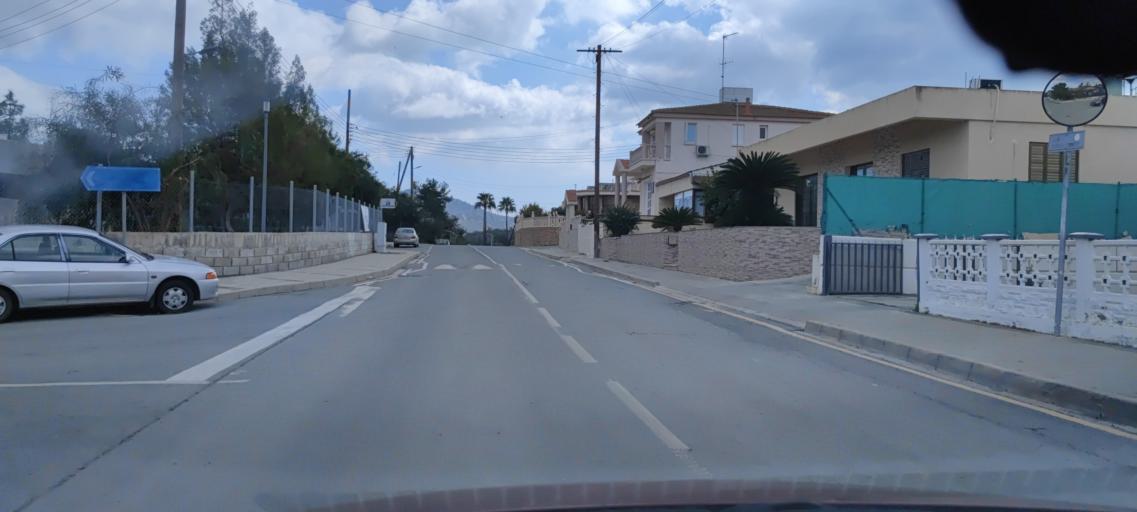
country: CY
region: Larnaka
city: Kornos
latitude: 34.9156
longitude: 33.4018
